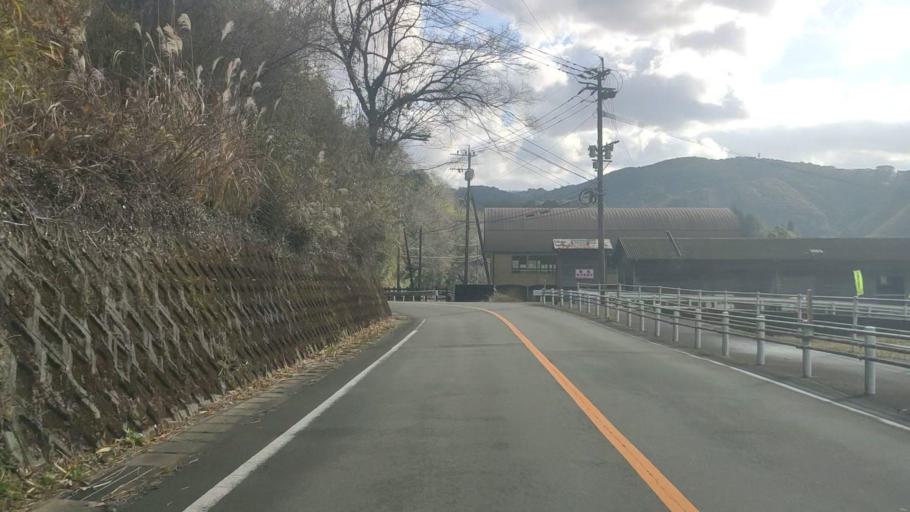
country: JP
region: Kumamoto
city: Hitoyoshi
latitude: 32.2911
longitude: 130.8430
